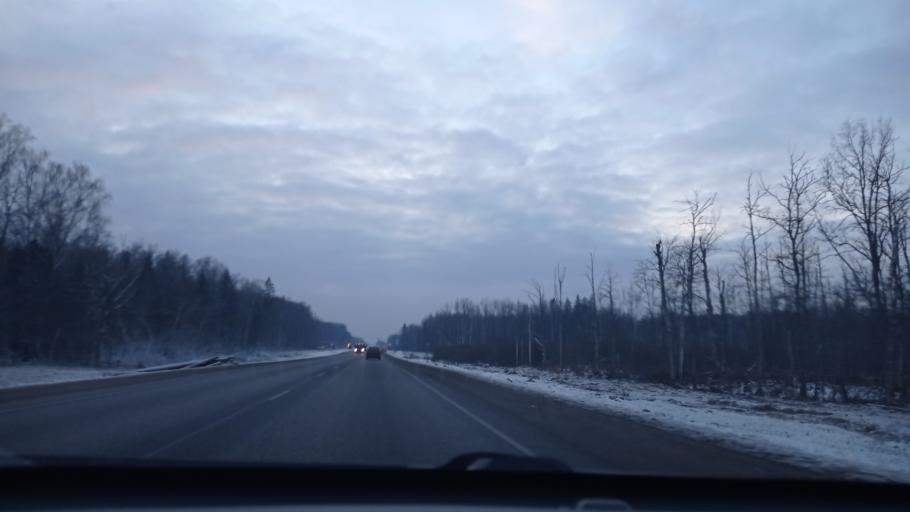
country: RU
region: Kaluga
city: Belousovo
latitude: 55.1247
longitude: 36.7481
